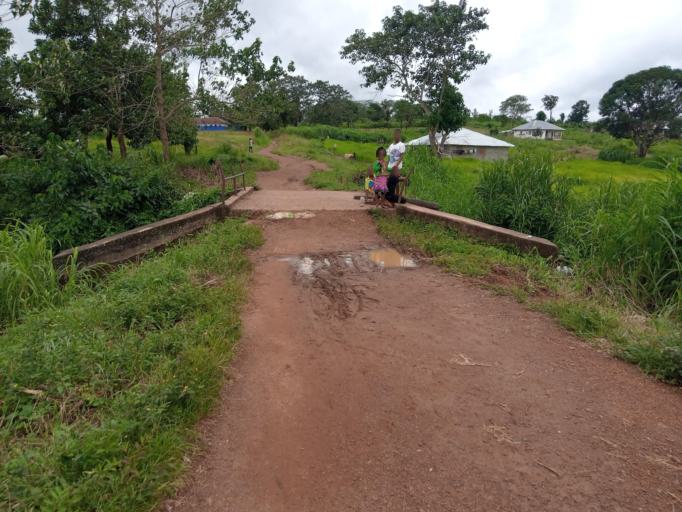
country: SL
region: Southern Province
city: Largo
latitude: 8.2008
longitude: -12.0553
